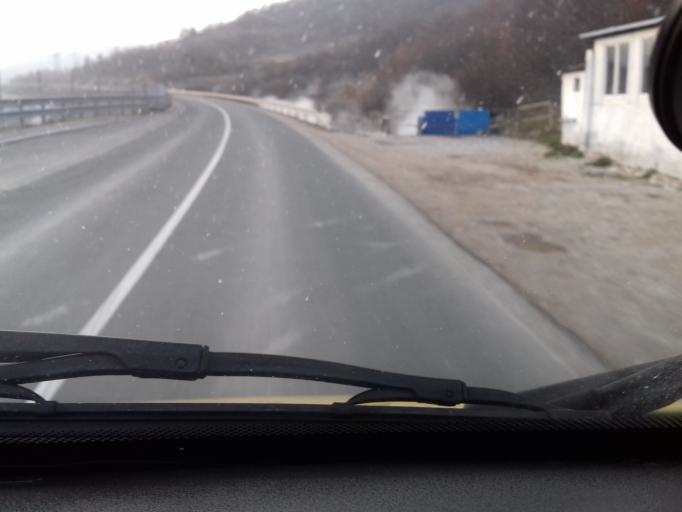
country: BA
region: Federation of Bosnia and Herzegovina
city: Kakanj
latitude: 44.1366
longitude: 18.0469
